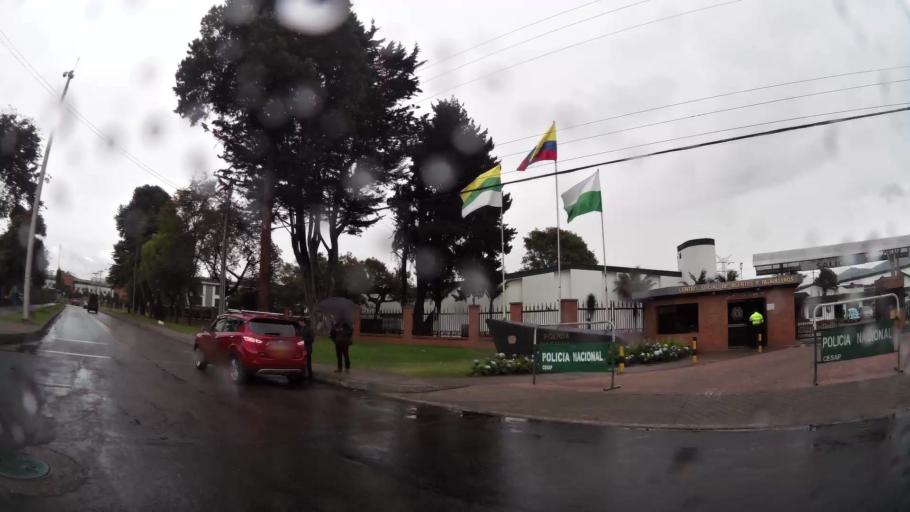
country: CO
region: Bogota D.C.
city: Bogota
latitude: 4.6571
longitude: -74.1035
